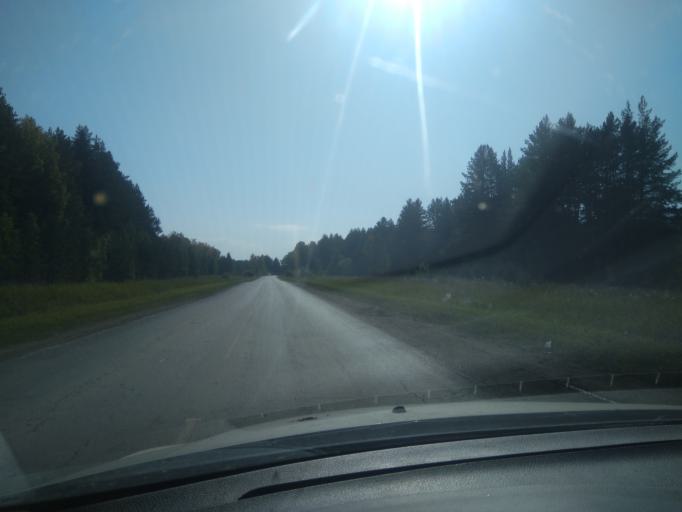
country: RU
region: Sverdlovsk
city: Pokrovskoye
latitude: 56.4514
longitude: 61.6023
